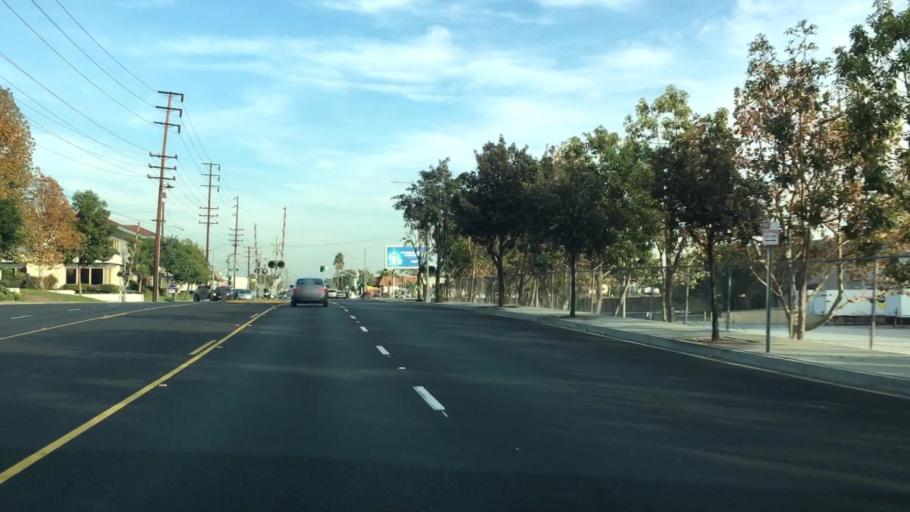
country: US
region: California
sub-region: Orange County
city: La Habra
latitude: 33.9246
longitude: -117.9263
